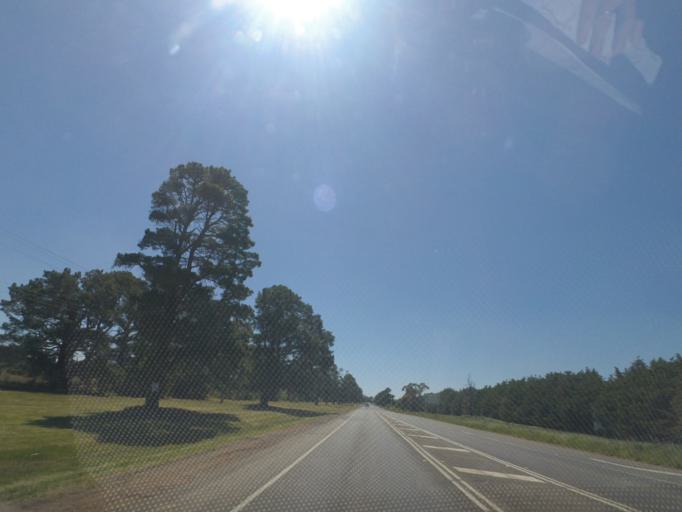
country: AU
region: Victoria
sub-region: Hume
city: Sunbury
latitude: -37.4126
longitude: 144.7489
